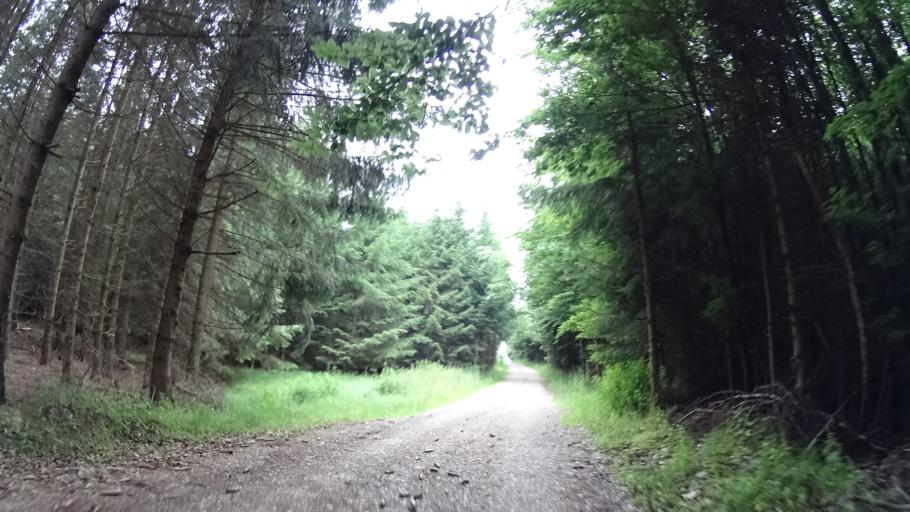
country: DE
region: Bavaria
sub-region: Upper Bavaria
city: Denkendorf
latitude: 48.8983
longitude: 11.4503
